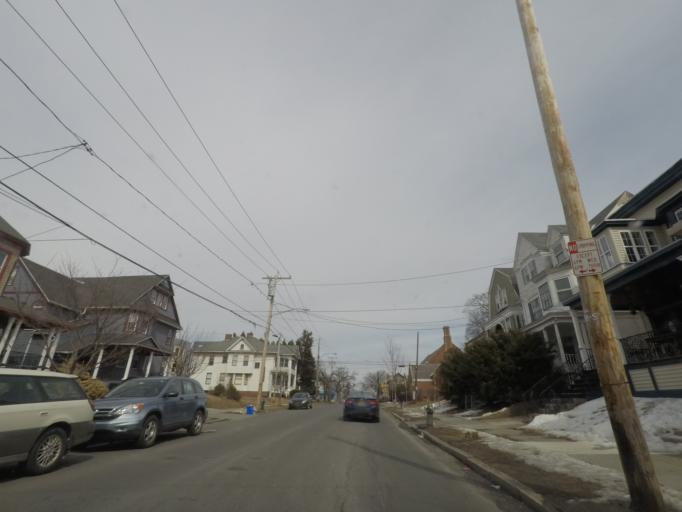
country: US
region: New York
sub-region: Albany County
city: West Albany
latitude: 42.6584
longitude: -73.7809
